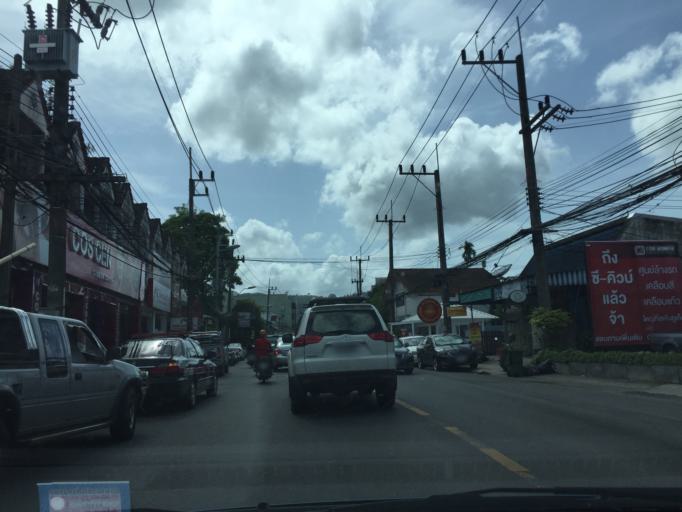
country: TH
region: Phuket
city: Wichit
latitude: 7.8996
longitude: 98.3827
